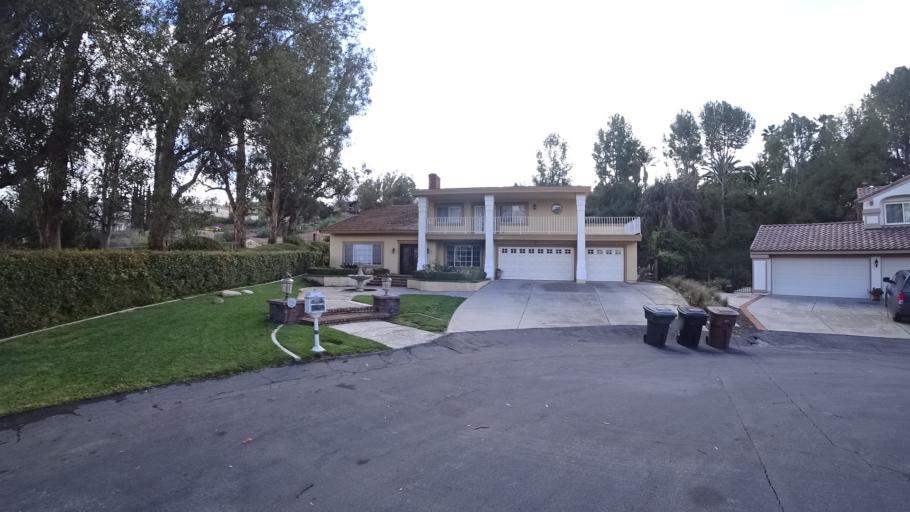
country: US
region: California
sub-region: Orange County
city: Villa Park
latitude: 33.8485
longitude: -117.7753
